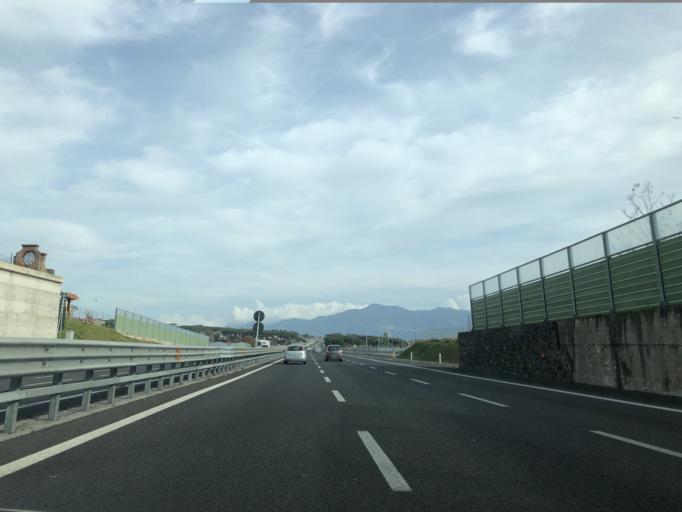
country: IT
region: Campania
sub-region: Provincia di Napoli
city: Torre del Greco
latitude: 40.7778
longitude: 14.3973
